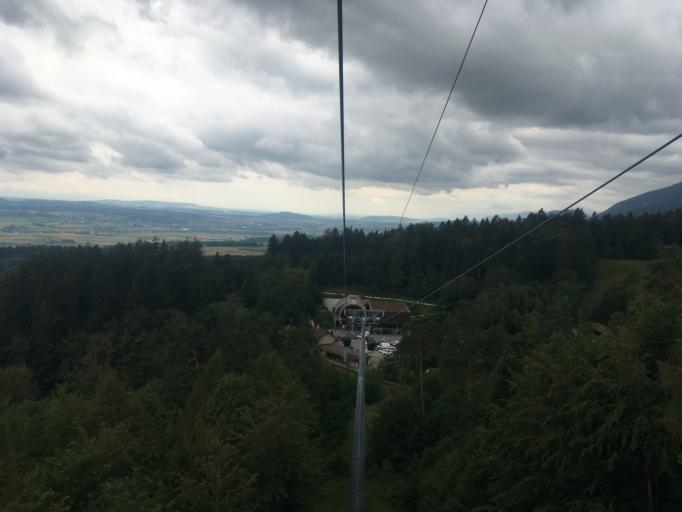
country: CH
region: Solothurn
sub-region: Bezirk Lebern
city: Langendorf
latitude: 47.2375
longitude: 7.4958
